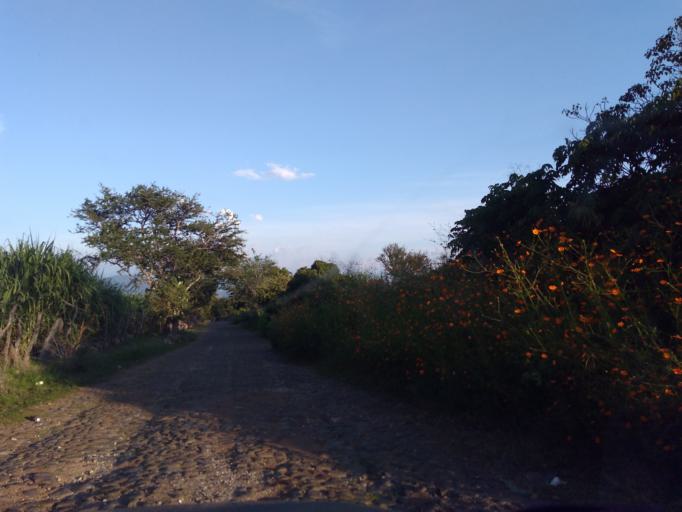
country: MX
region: Jalisco
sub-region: Tonila
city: San Marcos
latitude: 19.4600
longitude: -103.5230
